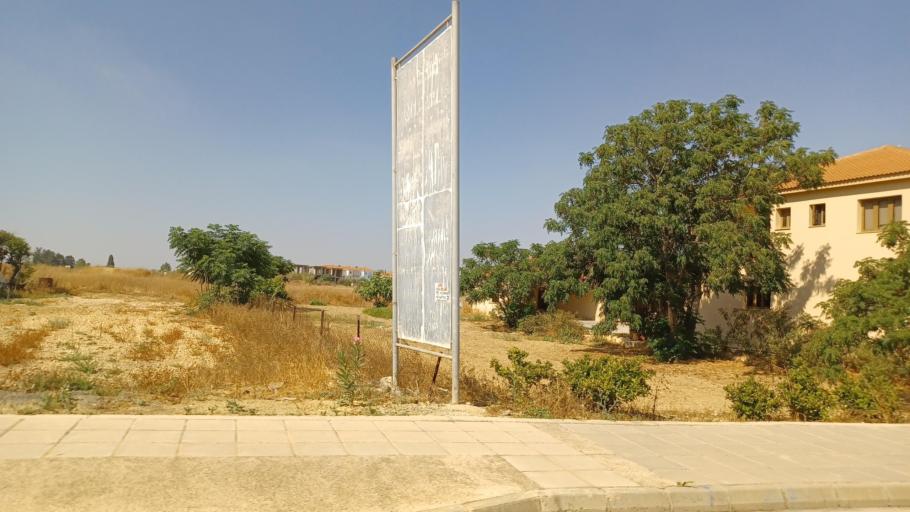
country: CY
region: Ammochostos
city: Acheritou
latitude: 35.0775
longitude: 33.8773
